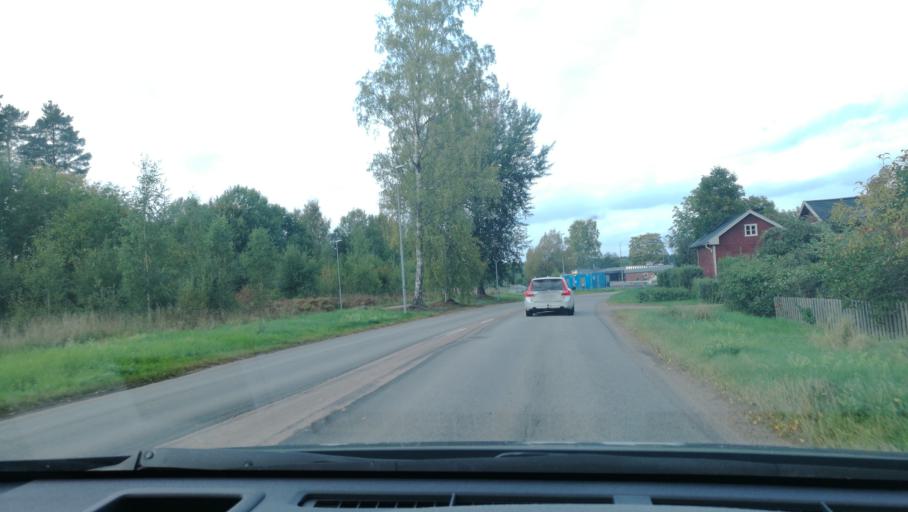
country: SE
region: Dalarna
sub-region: Avesta Kommun
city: Avesta
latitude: 60.1603
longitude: 16.1936
